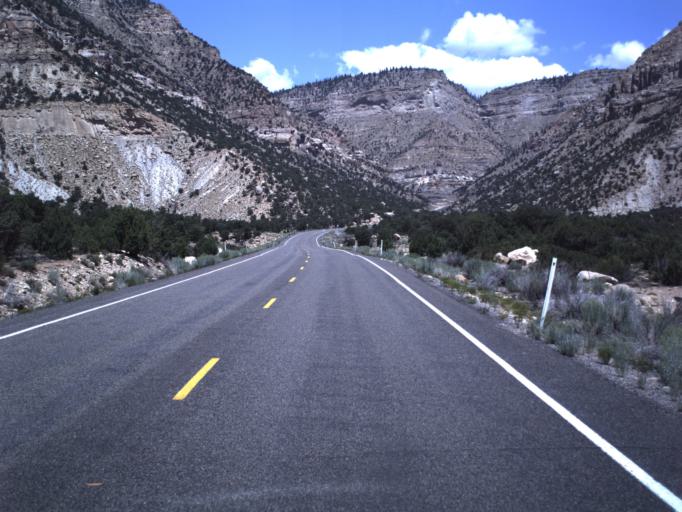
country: US
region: Utah
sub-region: Emery County
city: Orangeville
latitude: 39.3019
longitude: -111.1180
